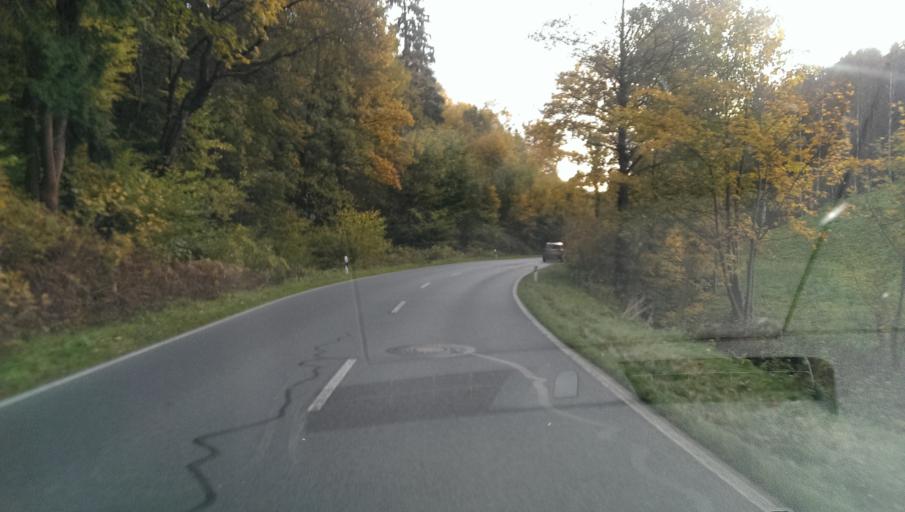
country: DE
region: Saxony
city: Sebnitz
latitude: 50.9744
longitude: 14.2601
